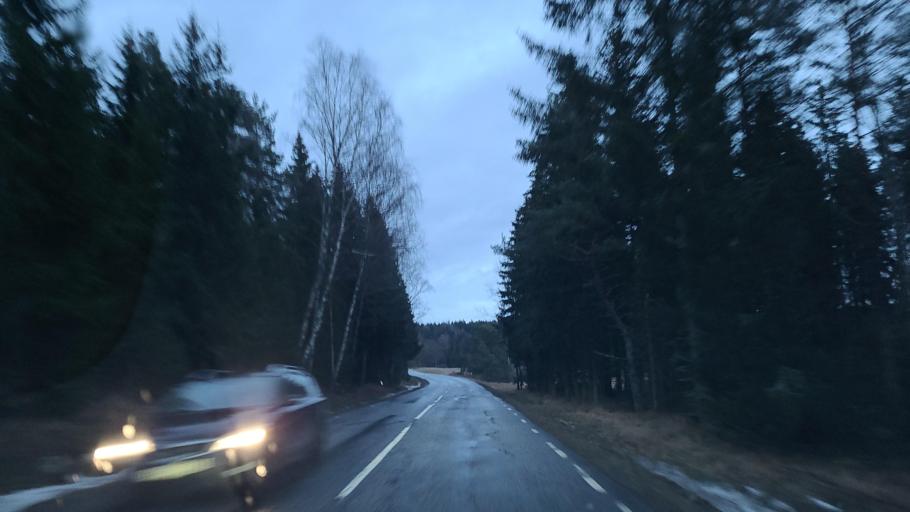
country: SE
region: Stockholm
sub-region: Norrtalje Kommun
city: Norrtalje
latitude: 59.7319
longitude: 18.5870
